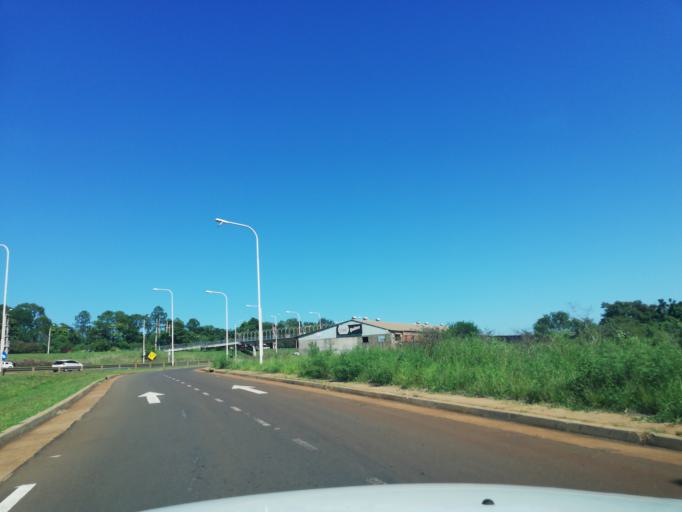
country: AR
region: Misiones
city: Garupa
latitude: -27.4598
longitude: -55.8223
